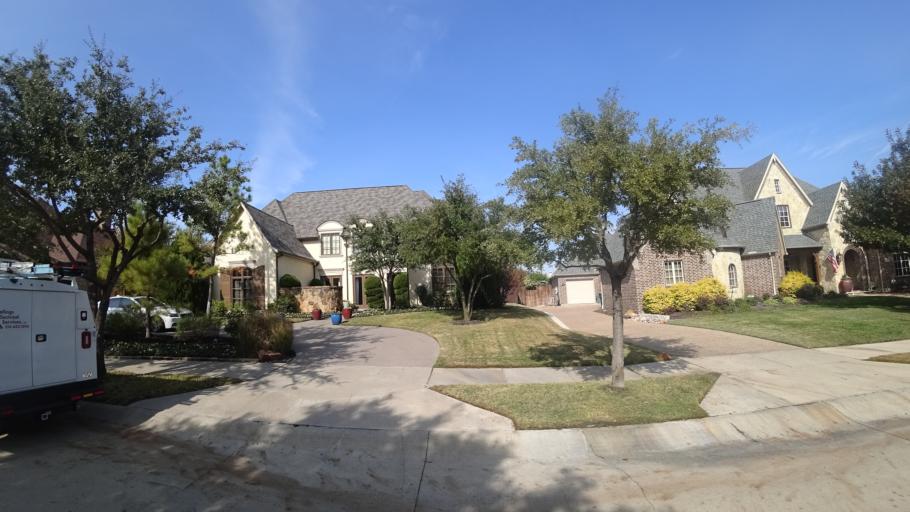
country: US
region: Texas
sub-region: Denton County
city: The Colony
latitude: 33.0387
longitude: -96.8932
